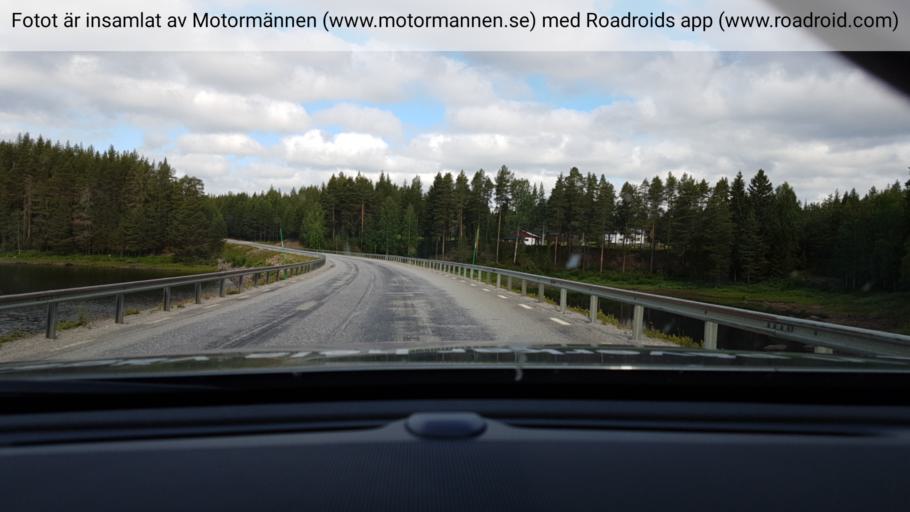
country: SE
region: Vaesterbotten
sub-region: Lycksele Kommun
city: Lycksele
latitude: 64.8509
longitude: 18.7578
